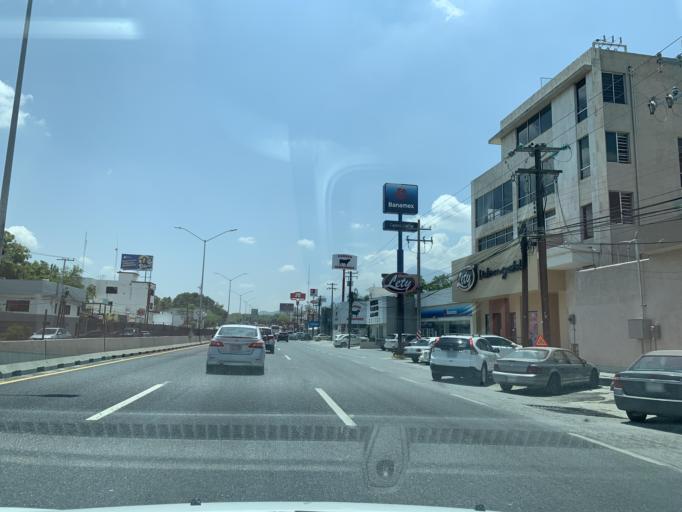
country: MX
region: Nuevo Leon
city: Santiago
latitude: 25.4043
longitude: -100.1335
